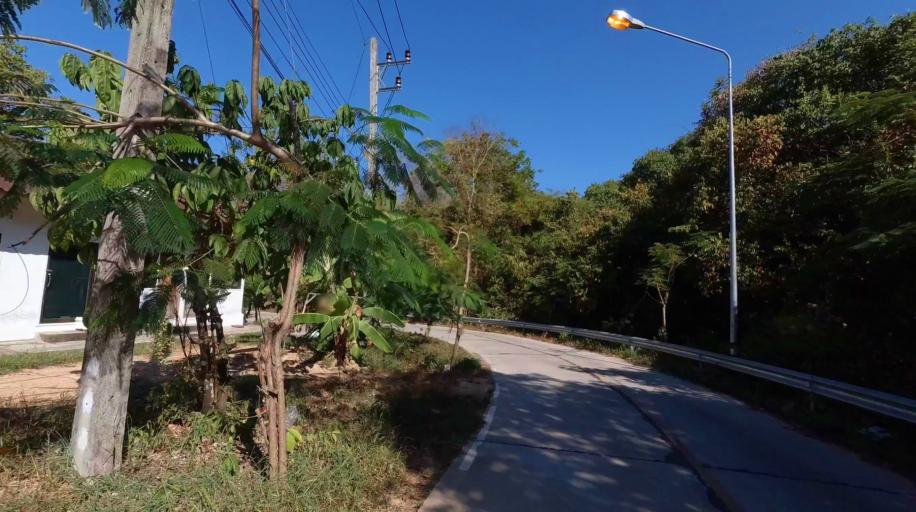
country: TH
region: Trat
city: Ko Kut
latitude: 11.6172
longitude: 102.5391
